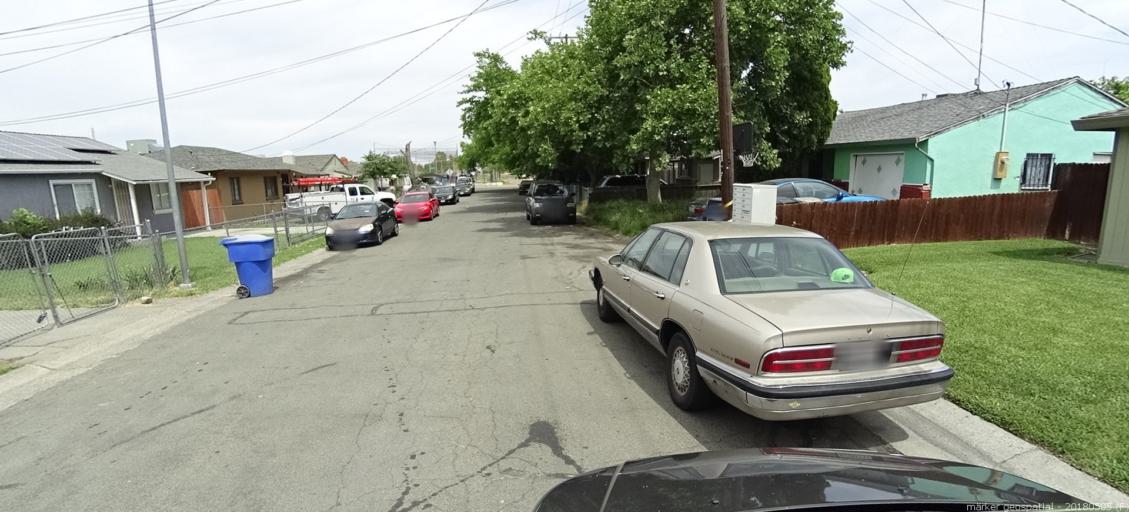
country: US
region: California
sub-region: Sacramento County
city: Rio Linda
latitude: 38.6340
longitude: -121.4311
